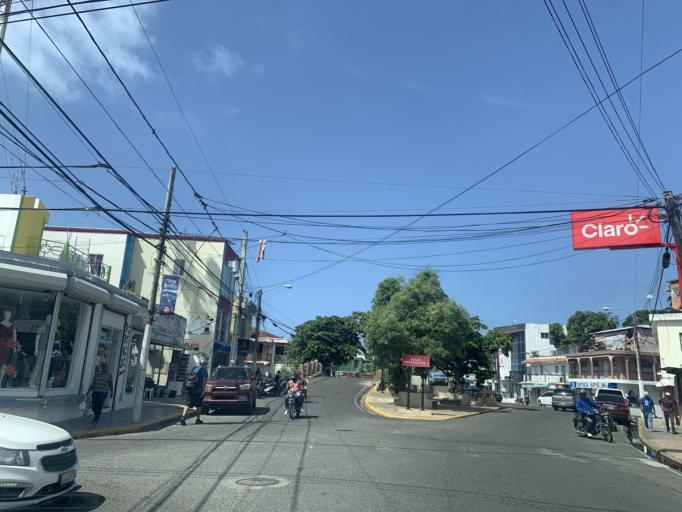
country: DO
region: Puerto Plata
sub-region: Puerto Plata
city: Puerto Plata
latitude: 19.7940
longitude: -70.6956
